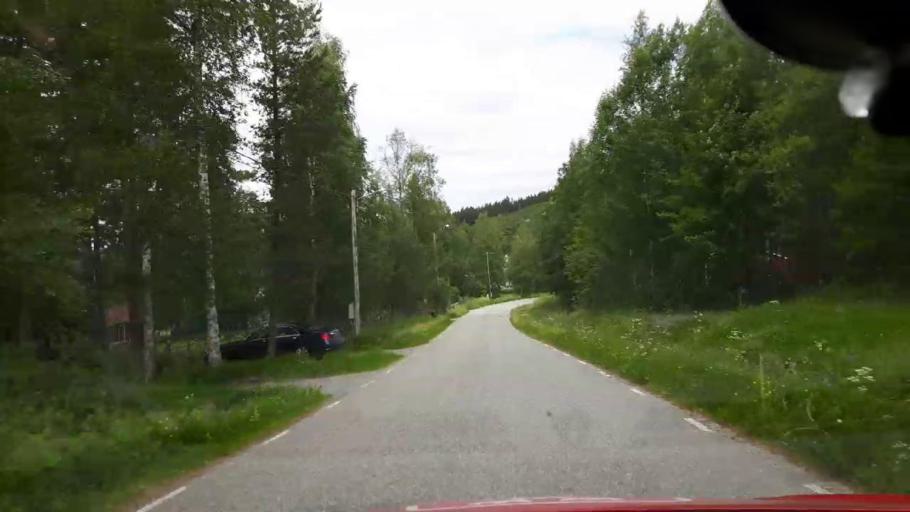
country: SE
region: Jaemtland
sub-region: Braecke Kommun
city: Braecke
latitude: 62.8838
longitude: 15.2726
